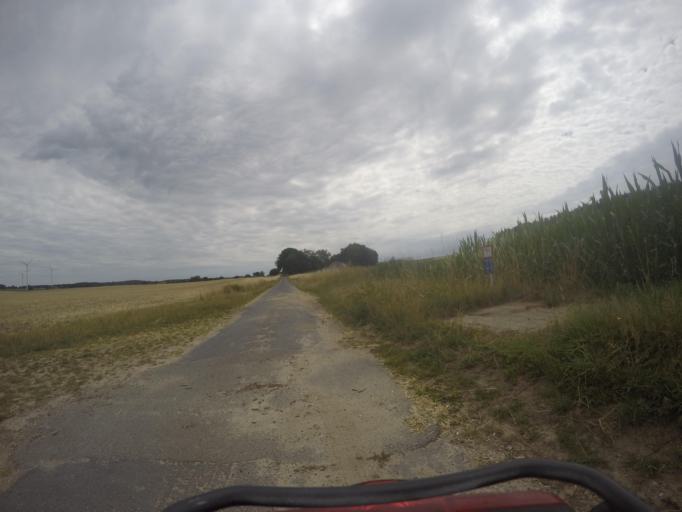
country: DE
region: Lower Saxony
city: Dahlem
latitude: 53.2167
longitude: 10.7444
